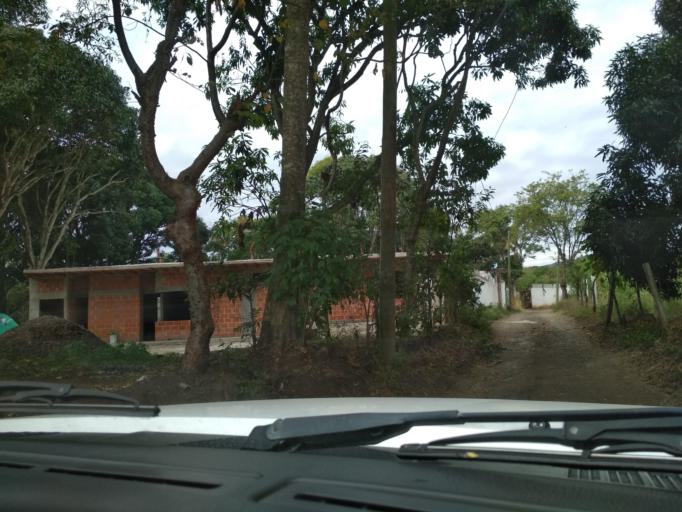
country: MX
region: Veracruz
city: Alto Lucero
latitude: 19.5921
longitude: -96.7826
